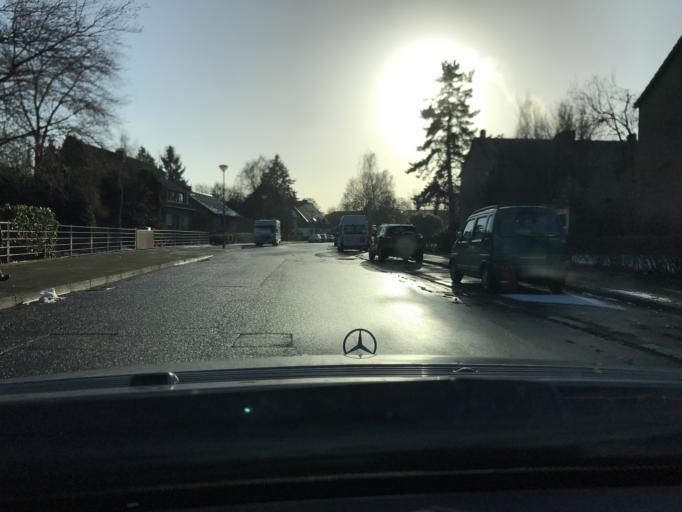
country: DE
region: North Rhine-Westphalia
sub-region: Regierungsbezirk Dusseldorf
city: Krefeld
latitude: 51.3513
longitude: 6.5540
